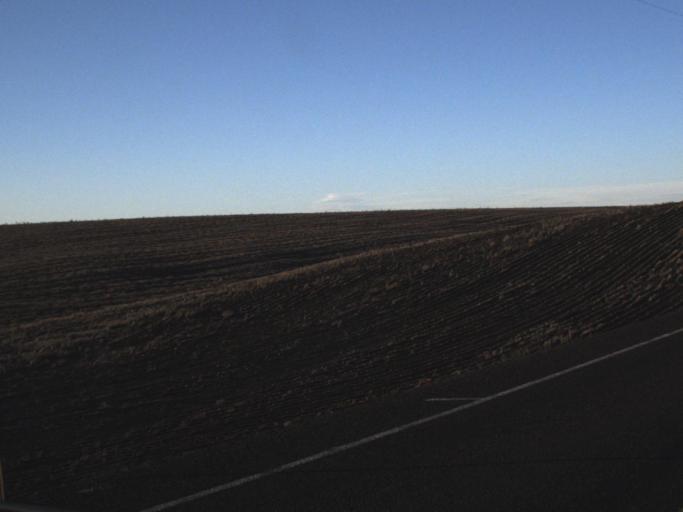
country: US
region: Washington
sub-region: Franklin County
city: Connell
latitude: 46.7484
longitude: -118.5476
